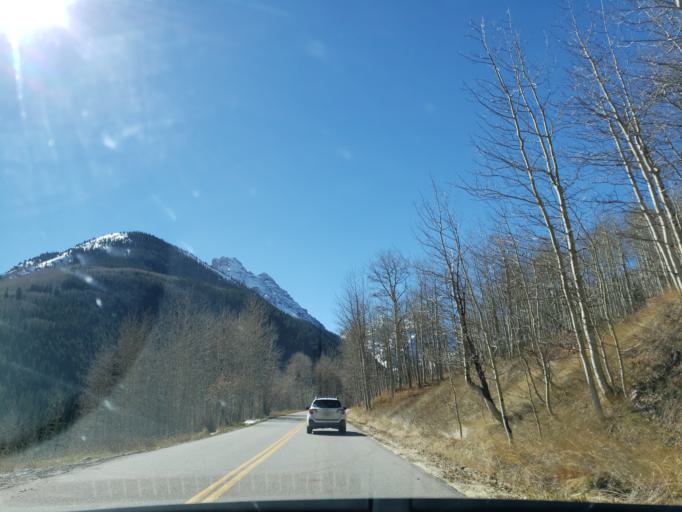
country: US
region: Colorado
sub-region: Pitkin County
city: Snowmass Village
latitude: 39.1085
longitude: -106.9180
